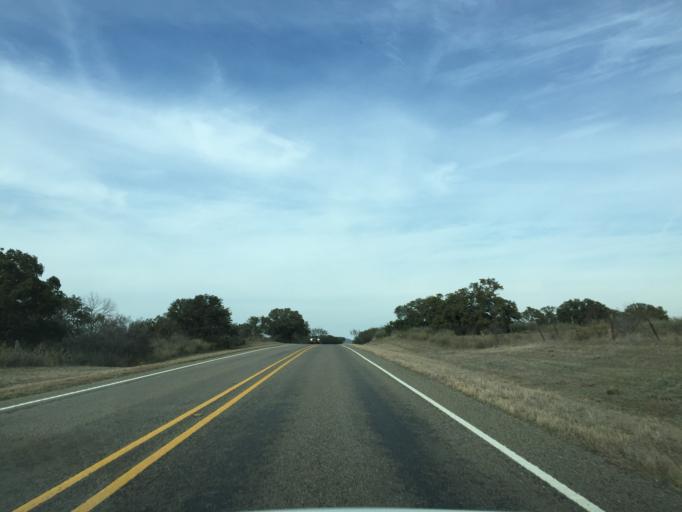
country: US
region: Texas
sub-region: Llano County
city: Llano
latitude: 30.5114
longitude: -98.7075
